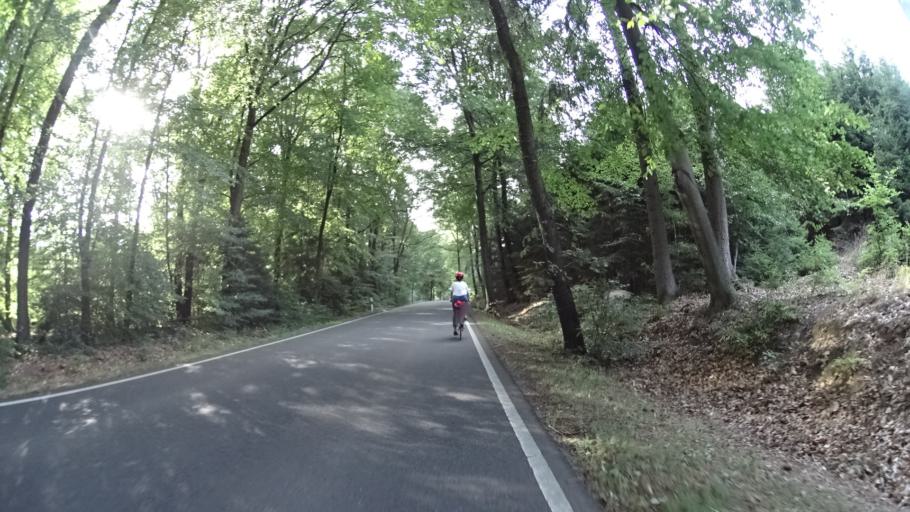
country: DE
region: Lower Saxony
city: Undeloh
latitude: 53.1612
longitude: 9.9005
